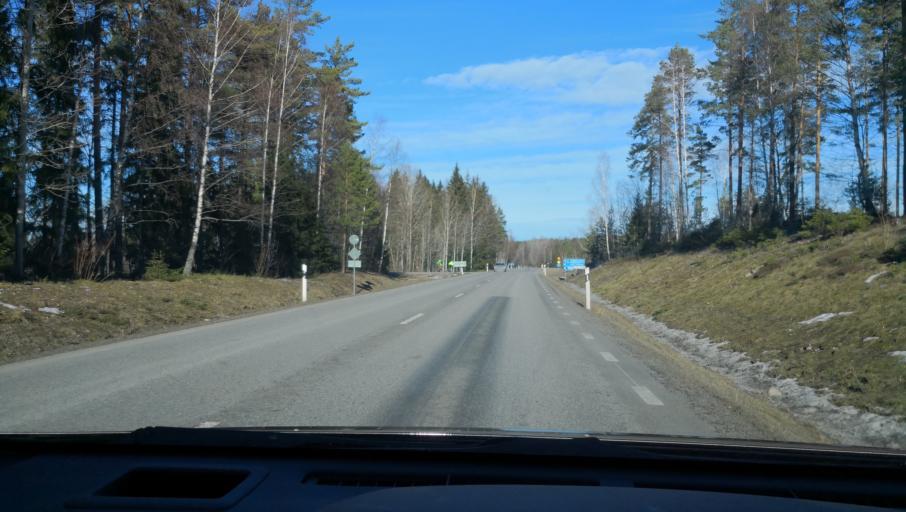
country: SE
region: Uppsala
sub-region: Uppsala Kommun
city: Vattholma
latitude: 60.0218
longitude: 17.7464
